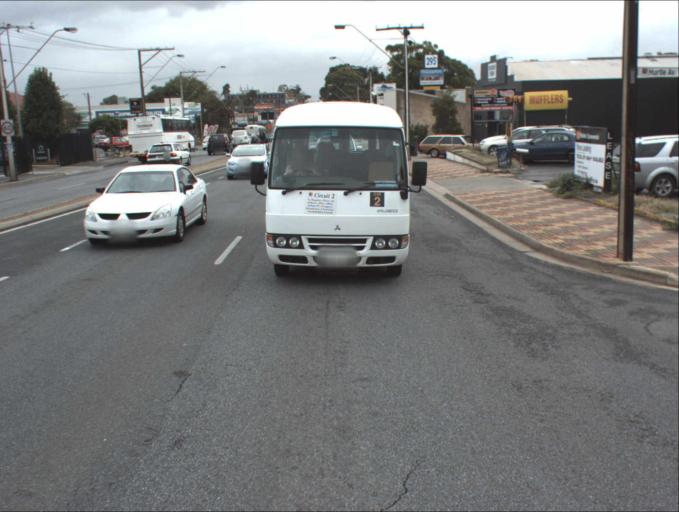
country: AU
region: South Australia
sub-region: Prospect
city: Prospect
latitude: -34.8720
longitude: 138.6019
